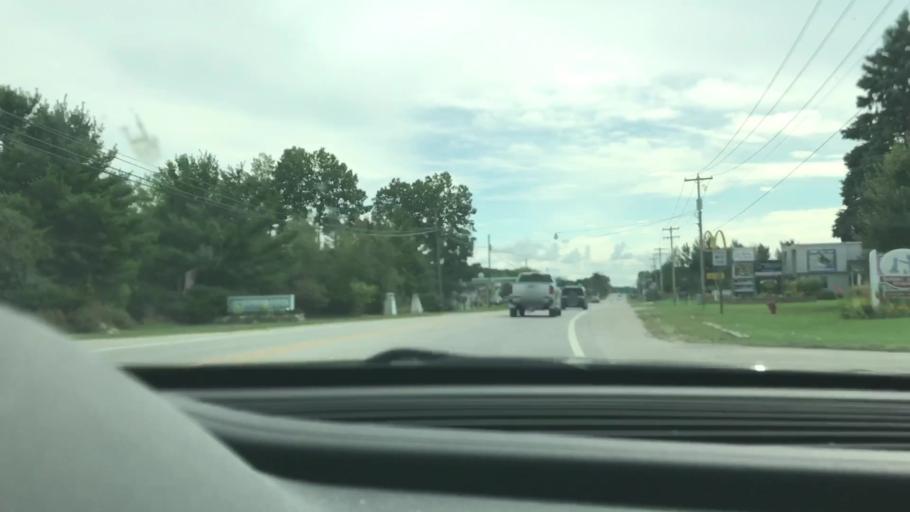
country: US
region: Michigan
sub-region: Antrim County
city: Bellaire
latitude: 44.9750
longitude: -85.1984
